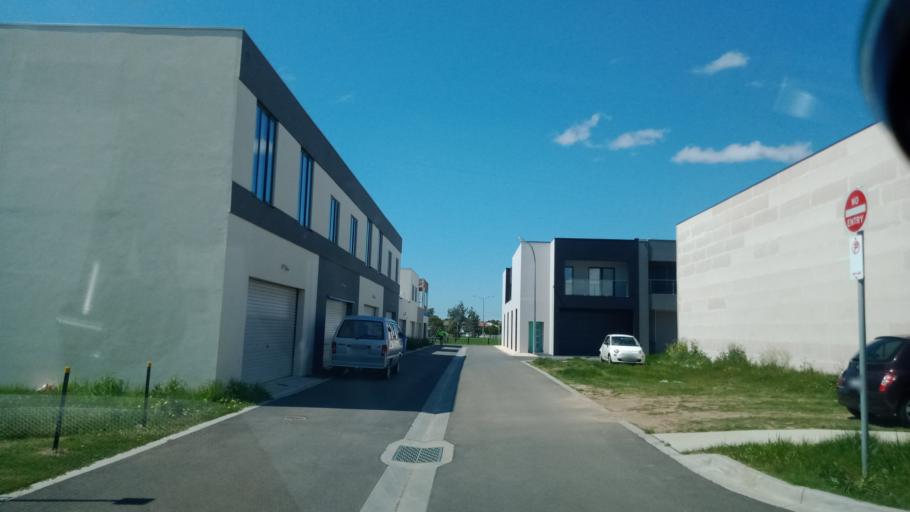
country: AU
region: Victoria
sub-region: Casey
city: Cranbourne West
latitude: -38.0908
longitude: 145.2534
